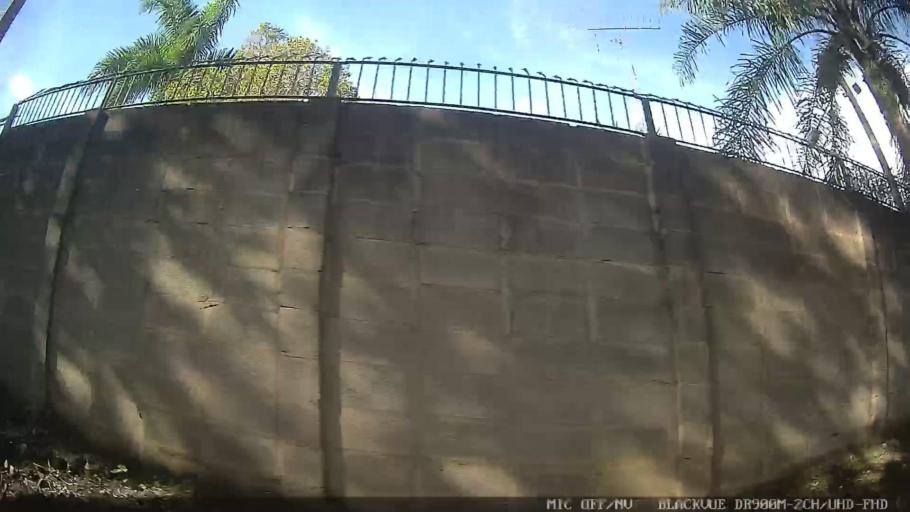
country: BR
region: Sao Paulo
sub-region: Tiete
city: Tiete
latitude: -23.0851
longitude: -47.6789
